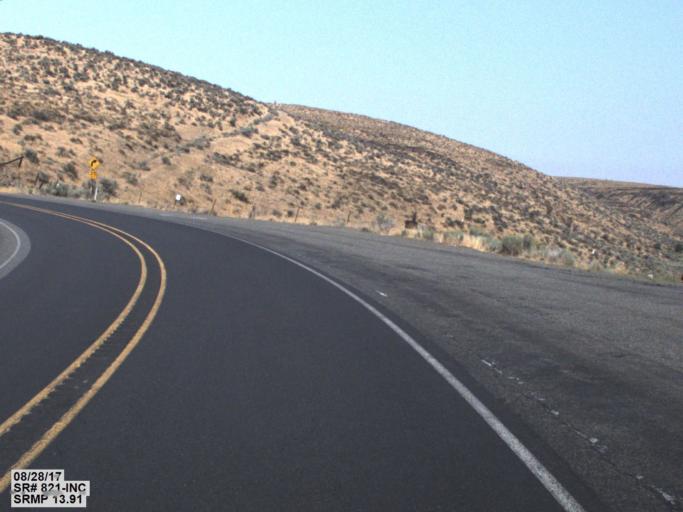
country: US
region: Washington
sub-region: Kittitas County
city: Kittitas
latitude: 46.8337
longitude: -120.4549
